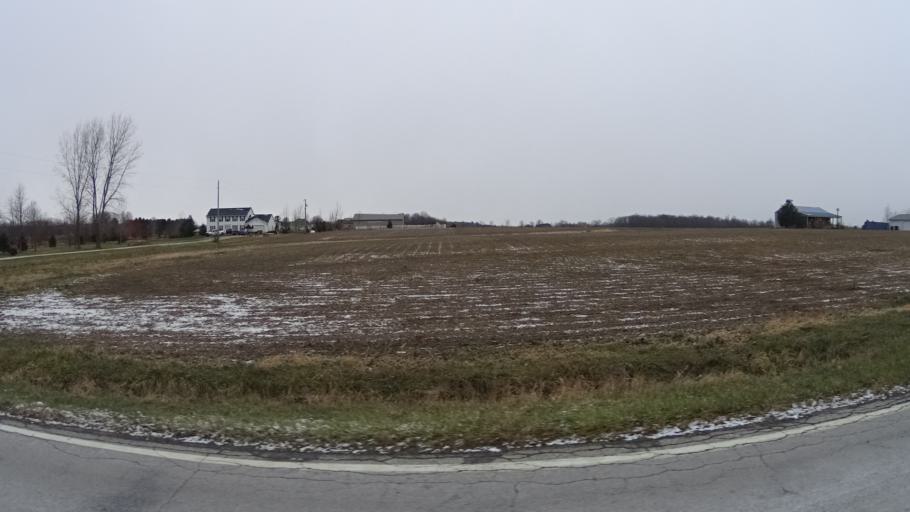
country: US
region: Ohio
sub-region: Lorain County
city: Lagrange
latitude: 41.1916
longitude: -82.1396
